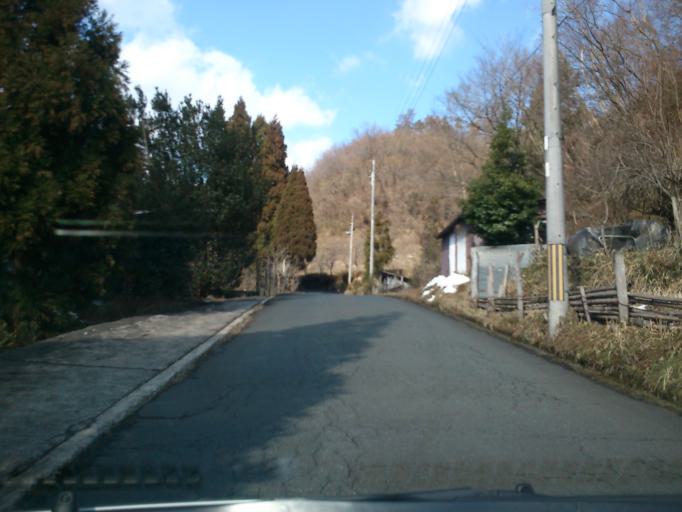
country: JP
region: Kyoto
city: Miyazu
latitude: 35.5852
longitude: 135.1775
